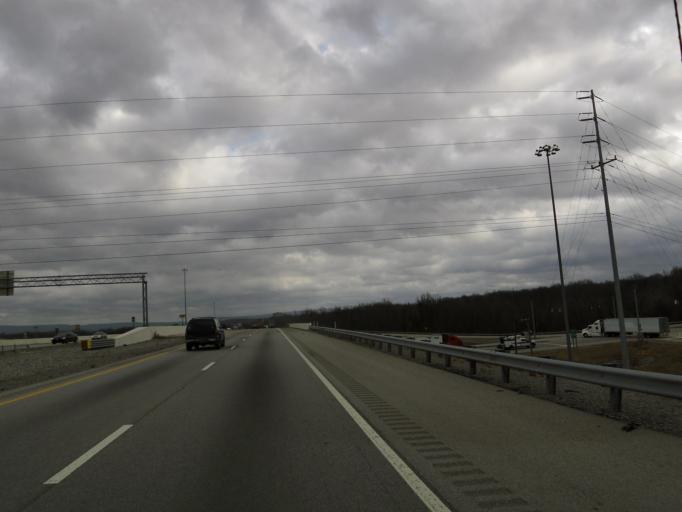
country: US
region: Tennessee
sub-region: Marion County
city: Kimball
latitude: 35.0405
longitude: -85.6920
